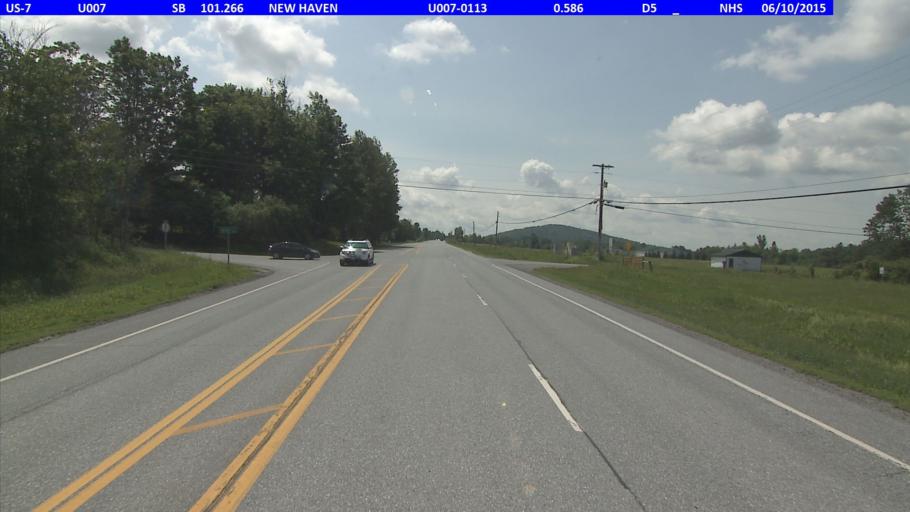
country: US
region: Vermont
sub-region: Addison County
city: Middlebury (village)
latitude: 44.0559
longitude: -73.1678
